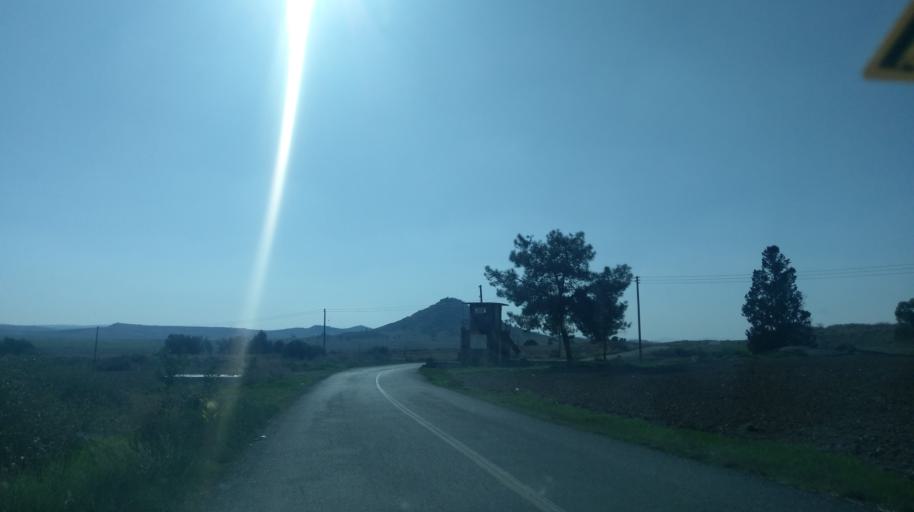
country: CY
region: Larnaka
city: Athienou
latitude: 35.0748
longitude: 33.4911
